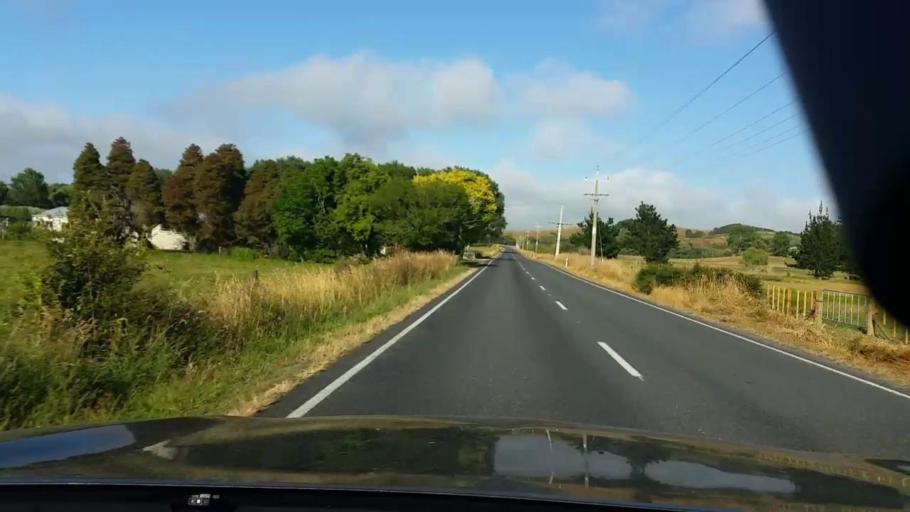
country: NZ
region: Waikato
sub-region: Hamilton City
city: Hamilton
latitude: -37.5923
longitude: 175.3699
